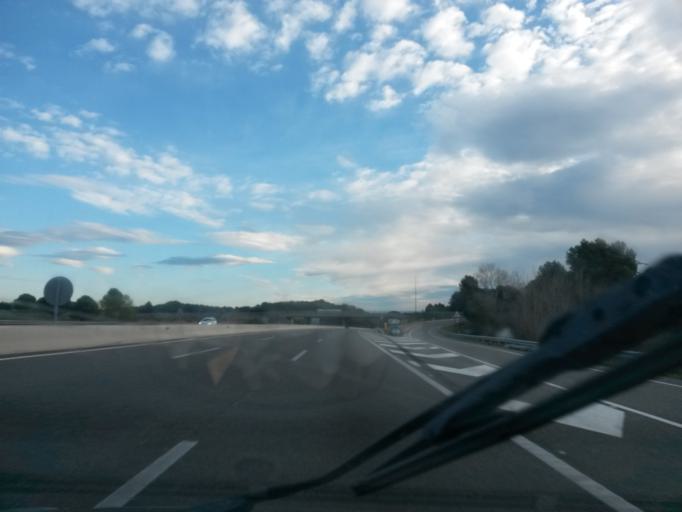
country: ES
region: Catalonia
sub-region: Provincia de Girona
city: Vilademuls
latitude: 42.1282
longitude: 2.9126
